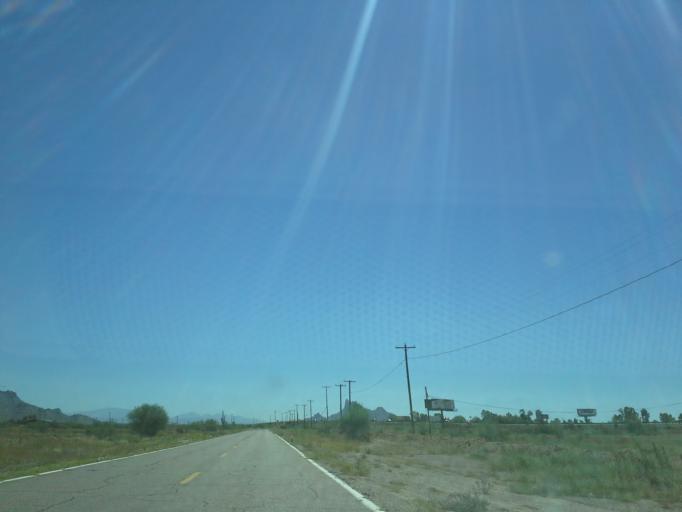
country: US
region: Arizona
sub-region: Pinal County
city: Eloy
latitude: 32.7180
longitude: -111.5047
